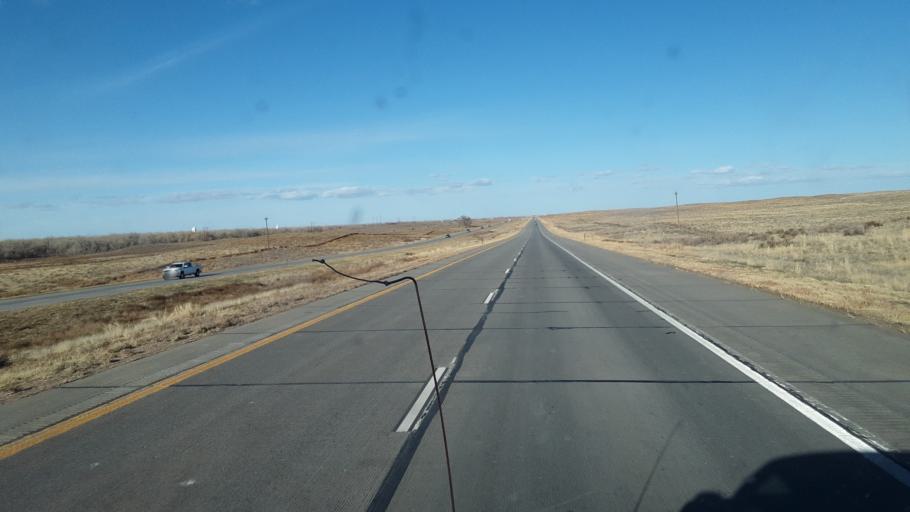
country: US
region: Colorado
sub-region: Logan County
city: Sterling
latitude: 40.5631
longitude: -103.2092
